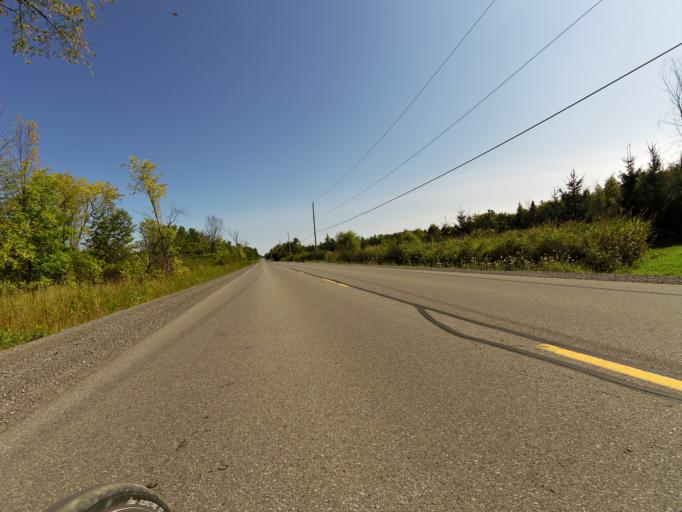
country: CA
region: Ontario
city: Bells Corners
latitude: 45.4350
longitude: -75.9654
